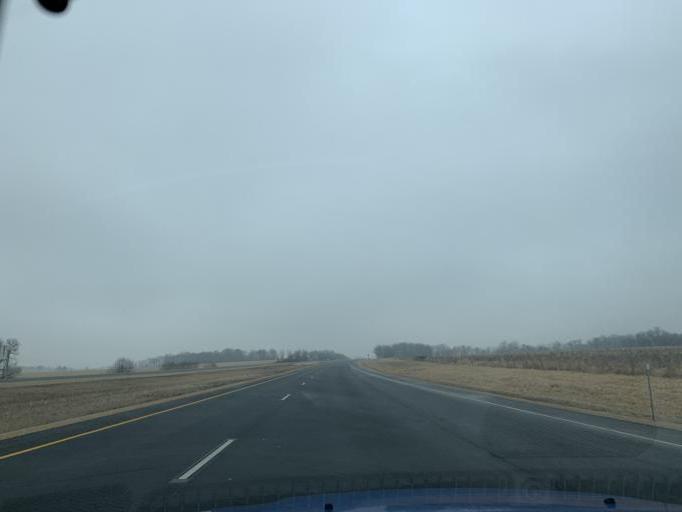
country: US
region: Wisconsin
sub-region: Dane County
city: Sun Prairie
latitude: 43.2441
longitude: -89.1425
